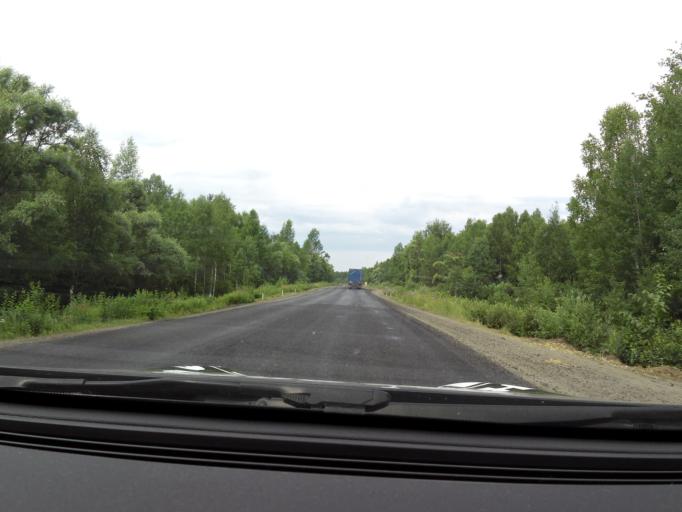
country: RU
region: Chelyabinsk
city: Asha
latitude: 54.8766
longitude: 57.2056
